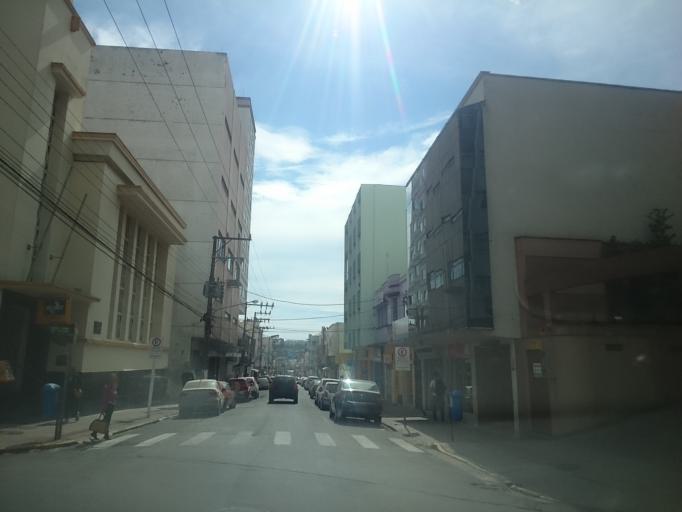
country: BR
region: Santa Catarina
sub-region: Lages
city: Lages
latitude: -27.8166
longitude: -50.3270
